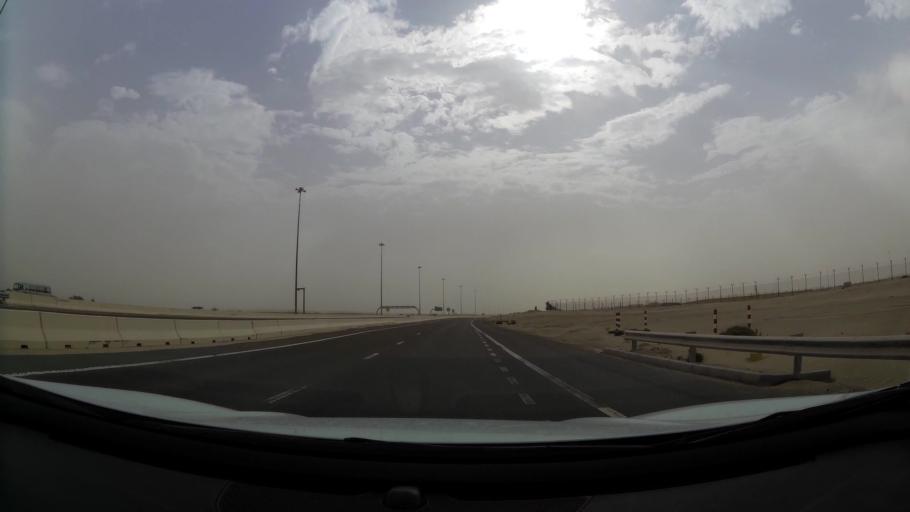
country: AE
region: Abu Dhabi
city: Abu Dhabi
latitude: 24.4808
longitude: 54.6584
